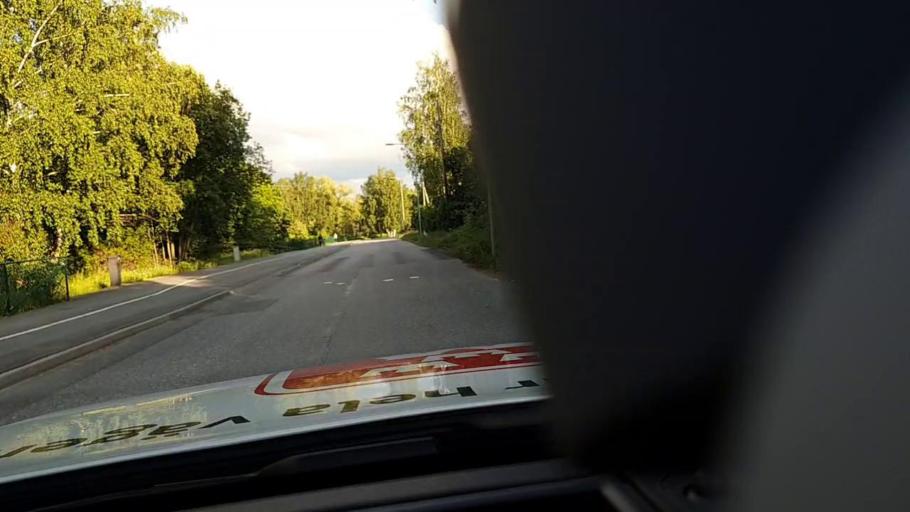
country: SE
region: Stockholm
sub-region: Huddinge Kommun
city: Huddinge
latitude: 59.2439
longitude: 17.9760
